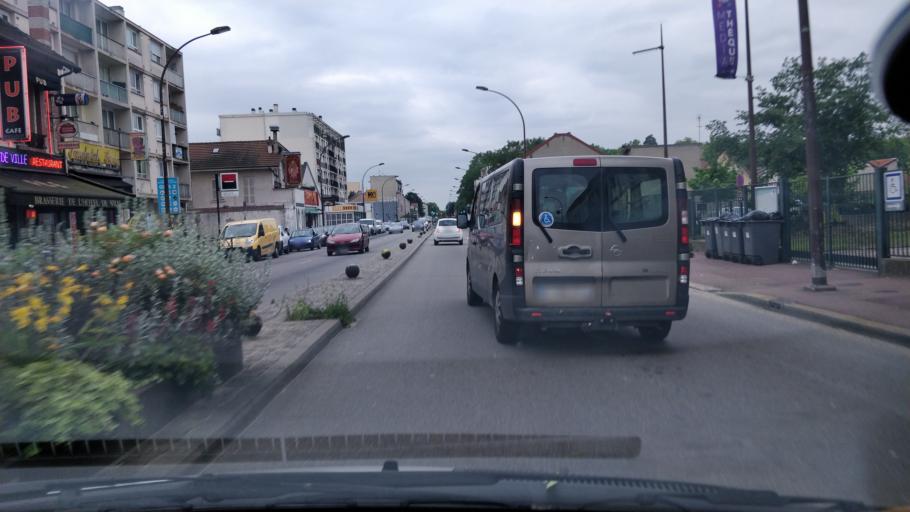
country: FR
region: Ile-de-France
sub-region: Departement de Seine-Saint-Denis
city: Livry-Gargan
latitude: 48.9187
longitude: 2.5367
